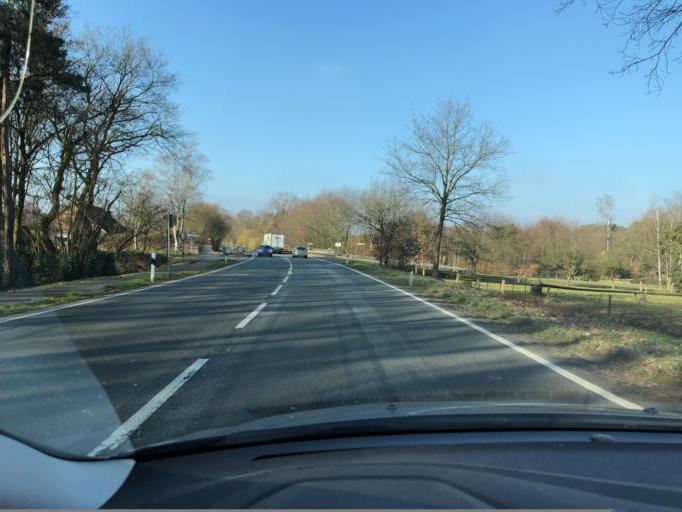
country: DE
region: Lower Saxony
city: Schwerinsdorf
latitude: 53.3068
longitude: 7.7677
